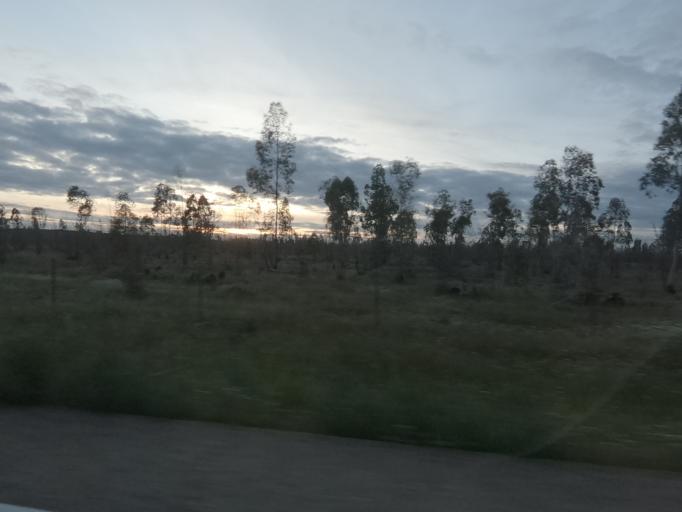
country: ES
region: Extremadura
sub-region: Provincia de Badajoz
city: Badajoz
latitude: 38.9845
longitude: -6.8806
